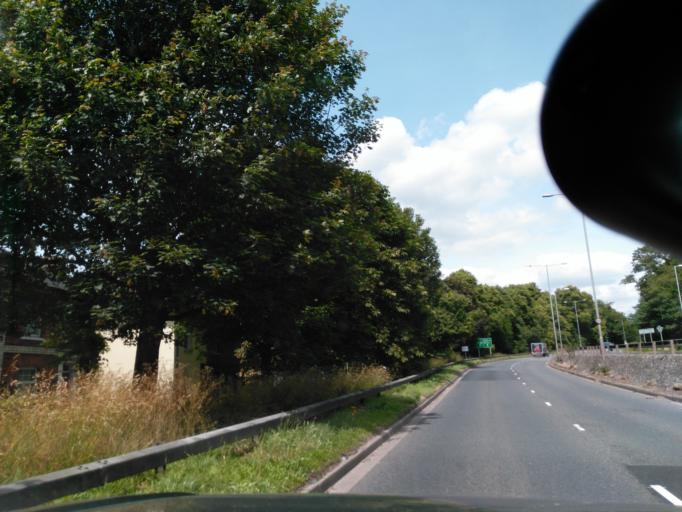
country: GB
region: England
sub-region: Wiltshire
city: Salisbury
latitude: 51.0701
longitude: -1.7899
